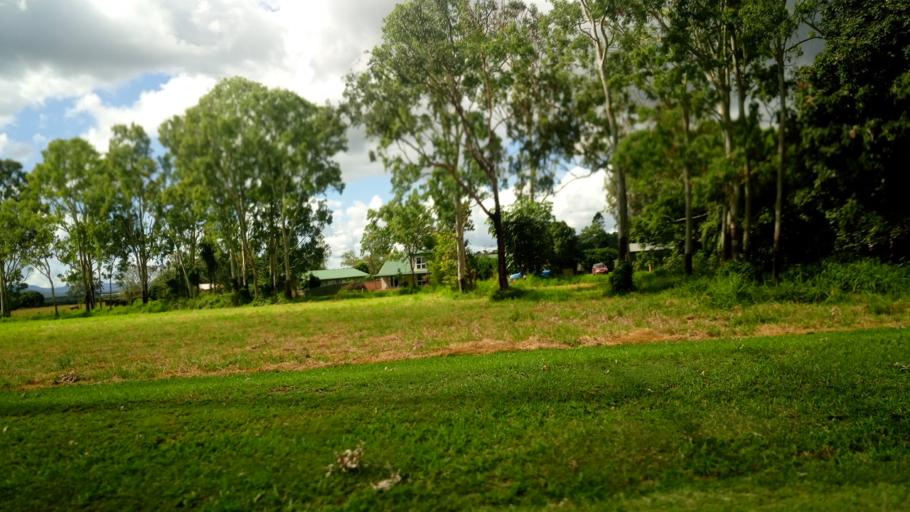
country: AU
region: Queensland
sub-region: Tablelands
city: Tolga
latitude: -17.2162
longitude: 145.4791
